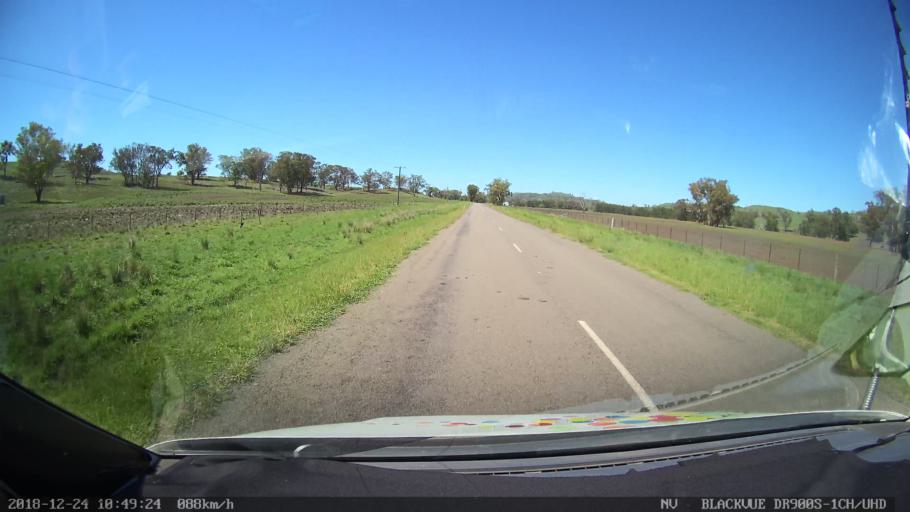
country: AU
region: New South Wales
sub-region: Upper Hunter Shire
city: Merriwa
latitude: -31.9471
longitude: 150.4276
